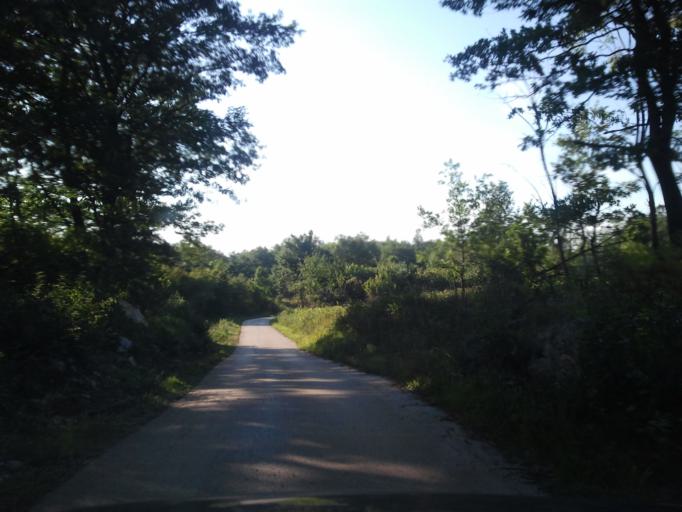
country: HR
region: Zadarska
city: Gracac
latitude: 44.3812
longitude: 15.7100
